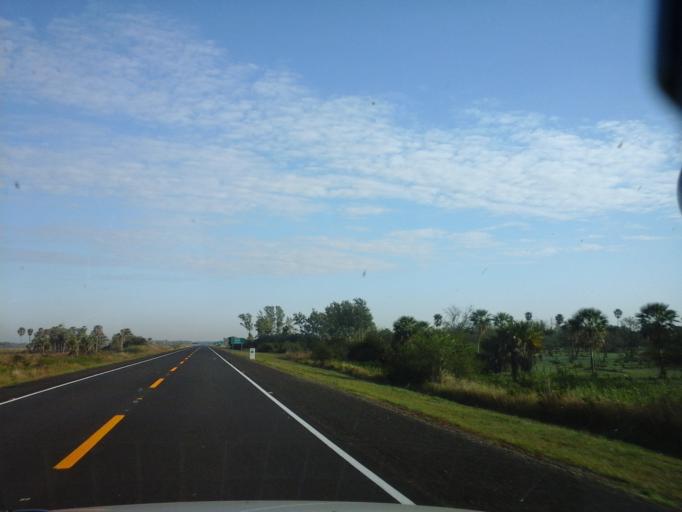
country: PY
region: Neembucu
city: Cerrito
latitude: -26.8820
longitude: -57.7402
